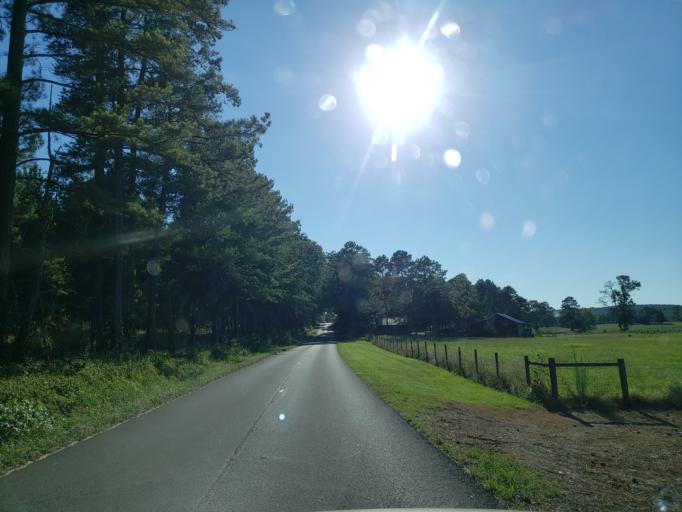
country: US
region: Georgia
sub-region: Polk County
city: Aragon
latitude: 34.1227
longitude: -85.0230
